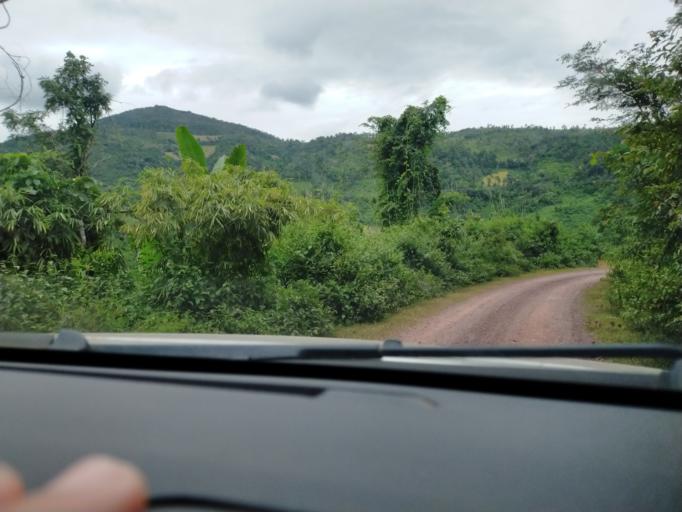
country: TH
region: Nan
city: Chaloem Phra Kiat
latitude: 19.7886
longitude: 101.3608
